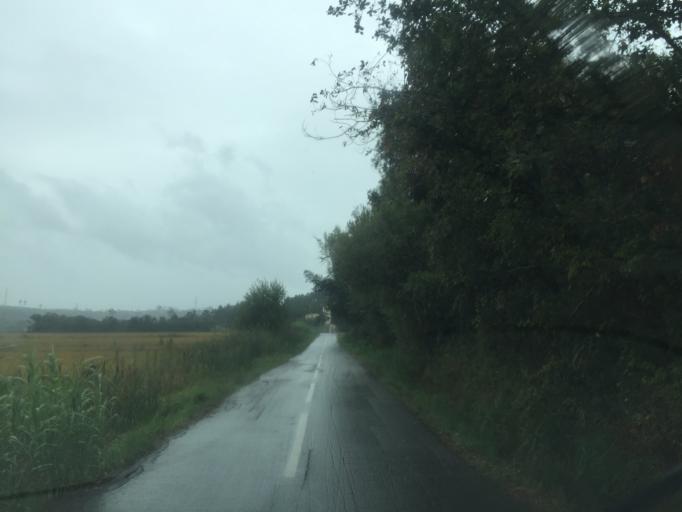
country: PT
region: Coimbra
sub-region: Figueira da Foz
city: Lavos
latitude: 40.0934
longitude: -8.8115
